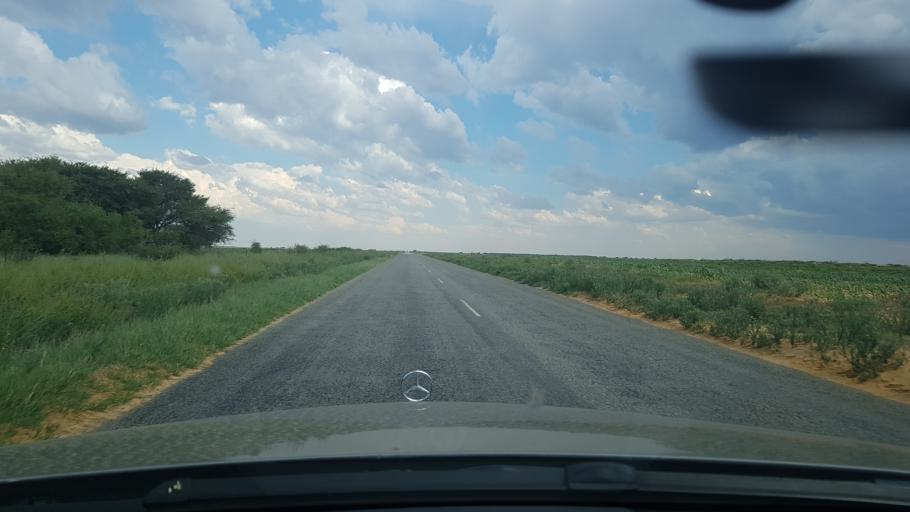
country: ZA
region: North-West
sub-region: Dr Ruth Segomotsi Mompati District Municipality
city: Bloemhof
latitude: -27.8759
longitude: 25.6612
